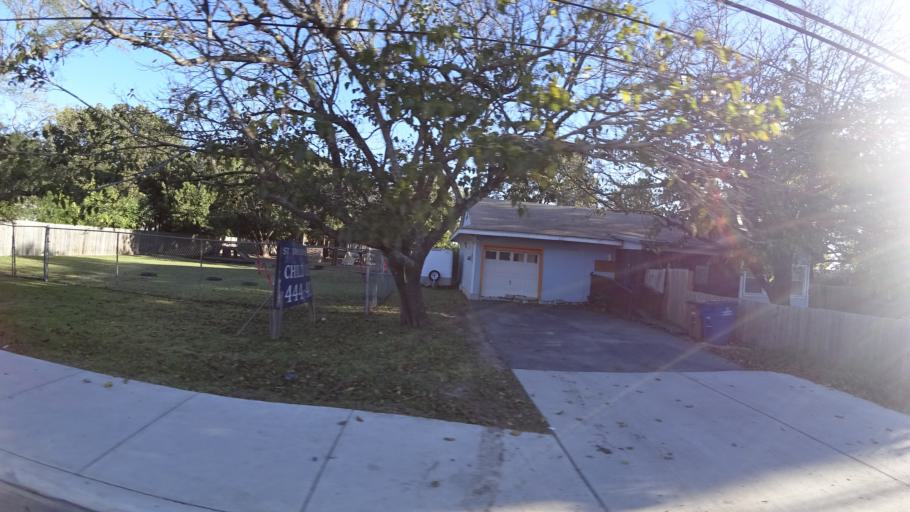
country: US
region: Texas
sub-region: Travis County
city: Austin
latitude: 30.2233
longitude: -97.7688
